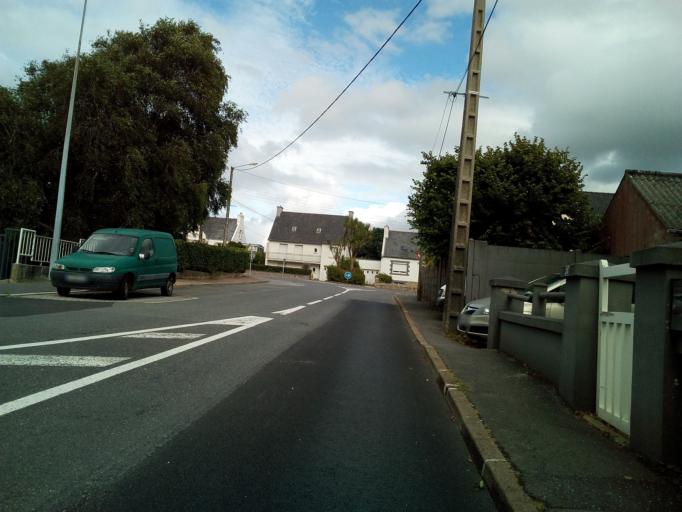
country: FR
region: Brittany
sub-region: Departement du Finistere
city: Landivisiau
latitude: 48.5143
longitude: -4.0642
